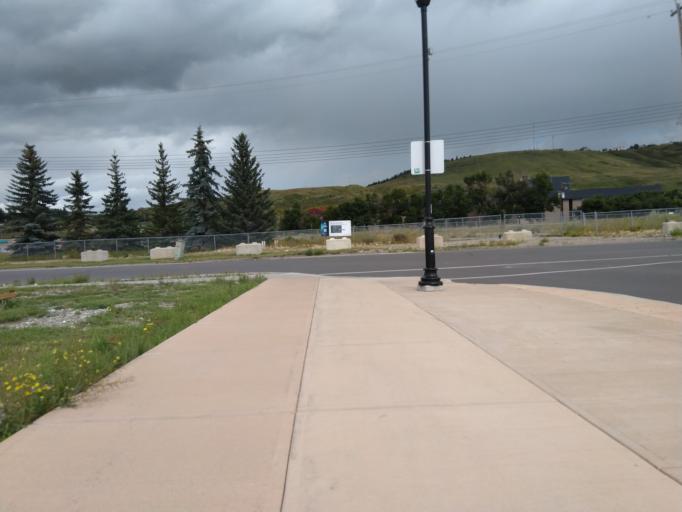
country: CA
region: Alberta
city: Cochrane
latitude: 51.1886
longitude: -114.4710
